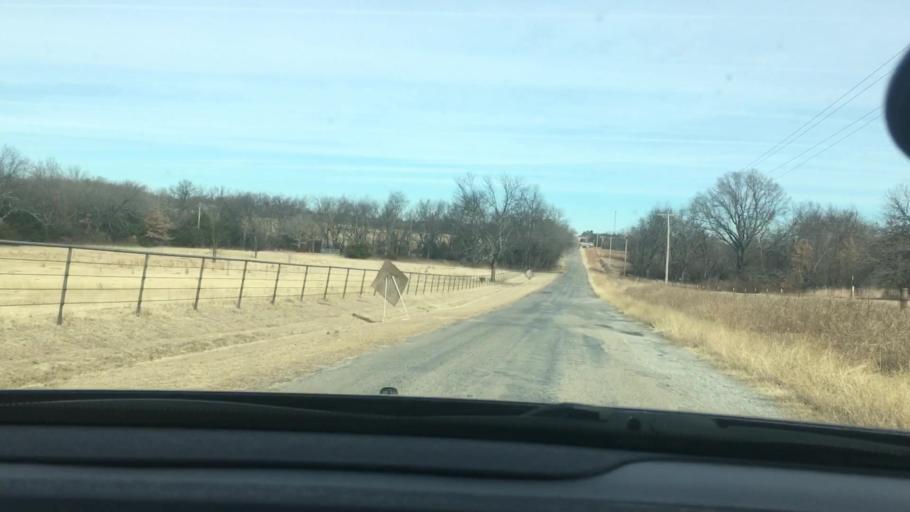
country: US
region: Oklahoma
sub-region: Garvin County
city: Wynnewood
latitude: 34.6393
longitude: -97.2475
